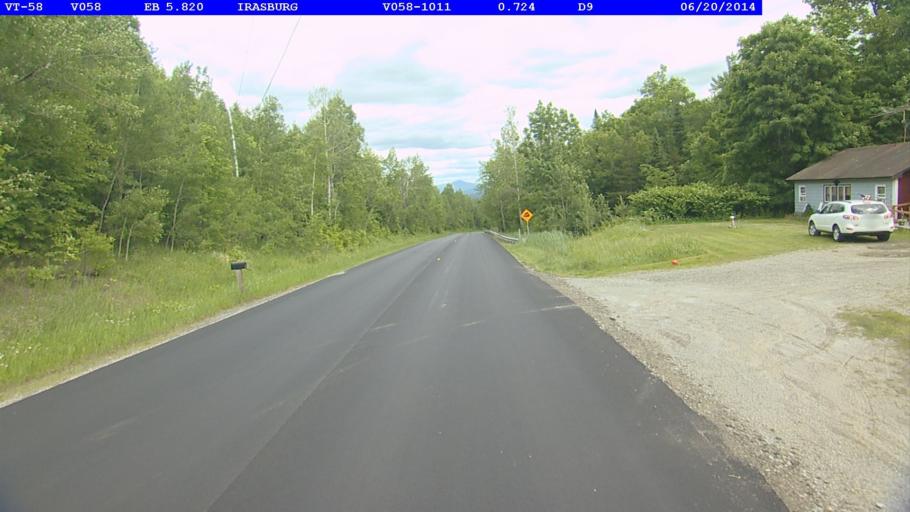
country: US
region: Vermont
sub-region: Orleans County
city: Newport
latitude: 44.8190
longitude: -72.3445
